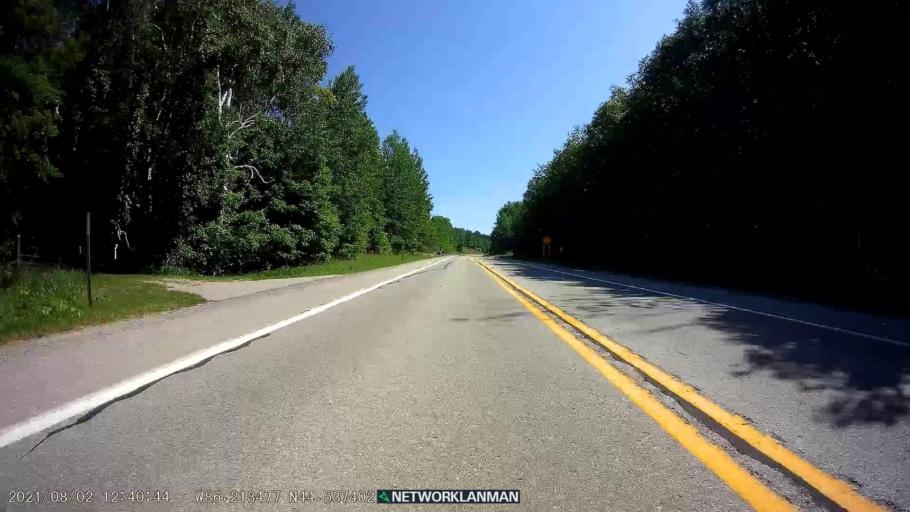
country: US
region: Michigan
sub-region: Benzie County
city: Frankfort
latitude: 44.5377
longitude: -86.2136
